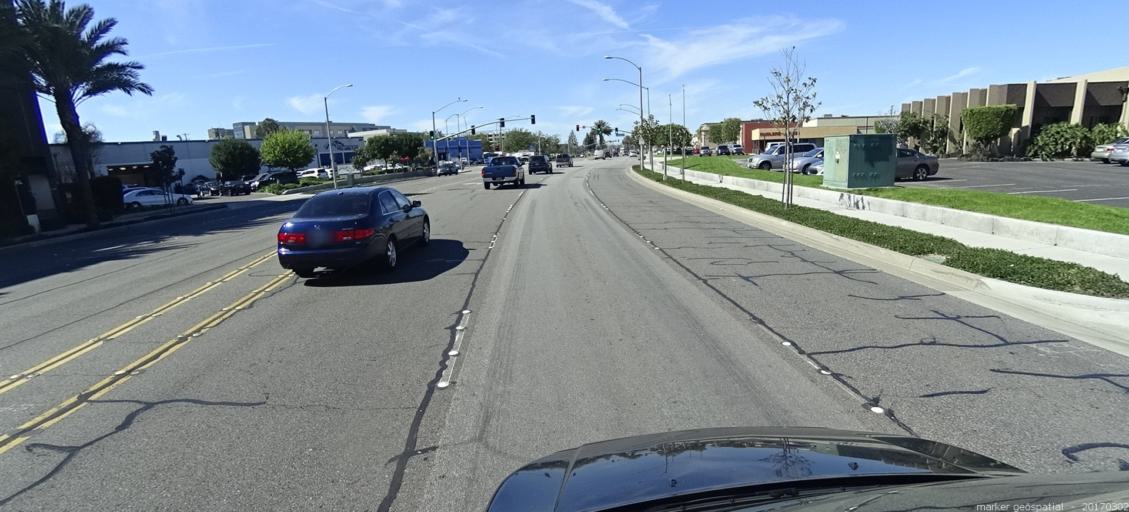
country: US
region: California
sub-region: Orange County
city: Placentia
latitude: 33.8553
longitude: -117.8414
